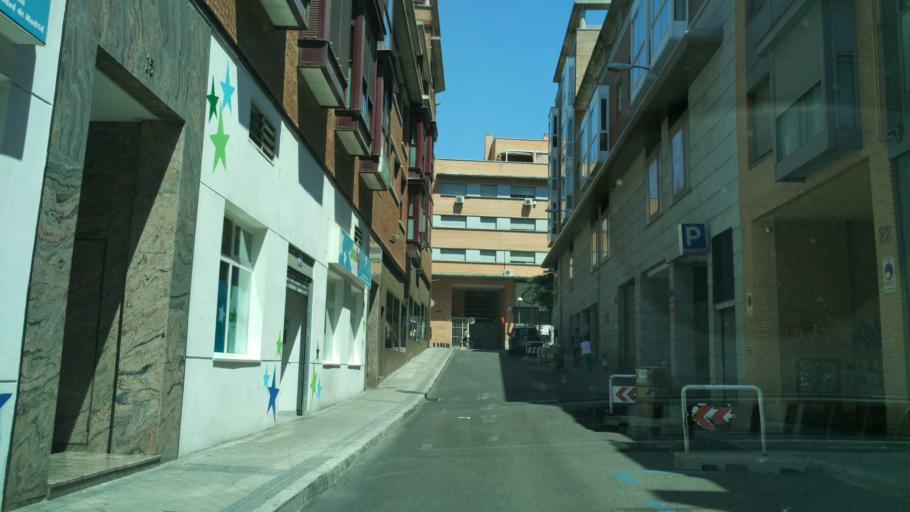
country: ES
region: Madrid
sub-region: Provincia de Madrid
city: Tetuan de las Victorias
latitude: 40.4581
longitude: -3.7027
